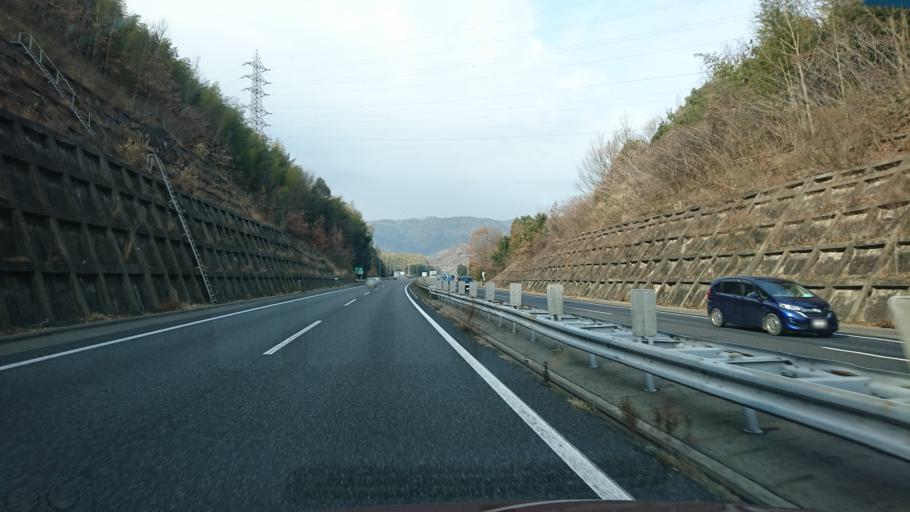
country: JP
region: Okayama
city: Kamogatacho-kamogata
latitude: 34.5665
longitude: 133.6484
